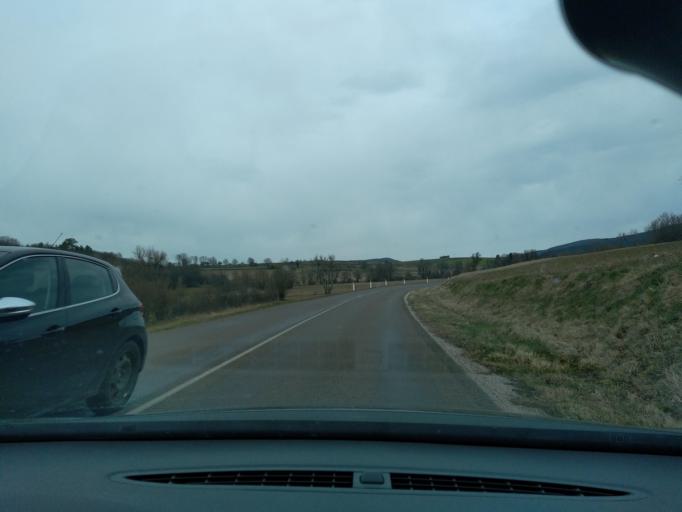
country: FR
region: Franche-Comte
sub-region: Departement du Jura
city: Arinthod
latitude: 46.4341
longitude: 5.5564
